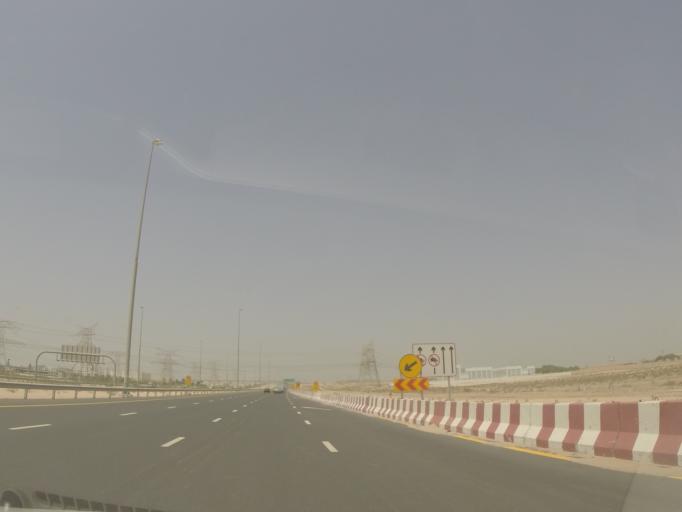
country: AE
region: Dubai
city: Dubai
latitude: 25.0066
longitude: 55.1714
